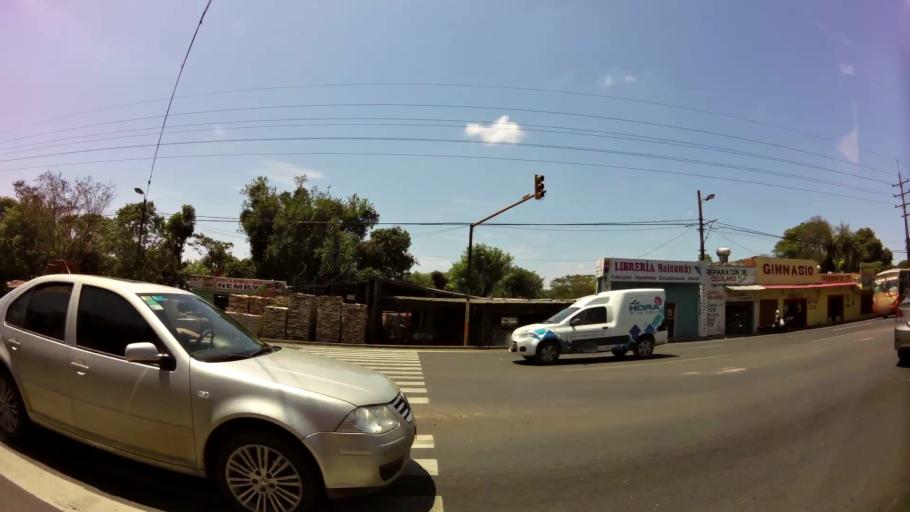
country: PY
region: Central
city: Nemby
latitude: -25.4047
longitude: -57.5427
